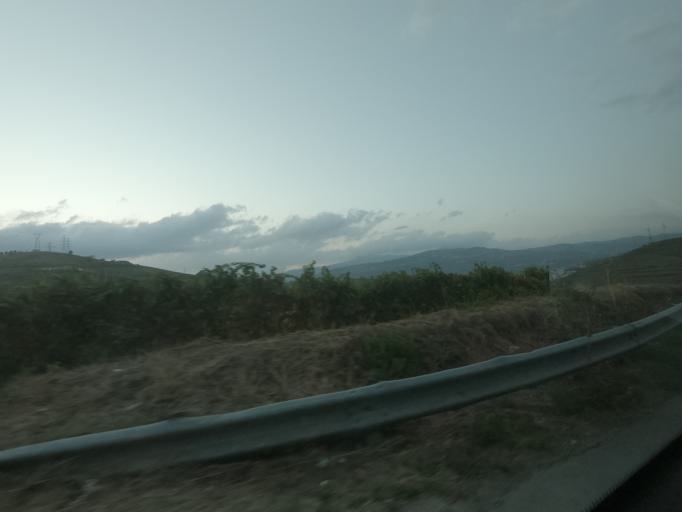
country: PT
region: Vila Real
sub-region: Peso da Regua
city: Peso da Regua
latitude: 41.1443
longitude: -7.7757
